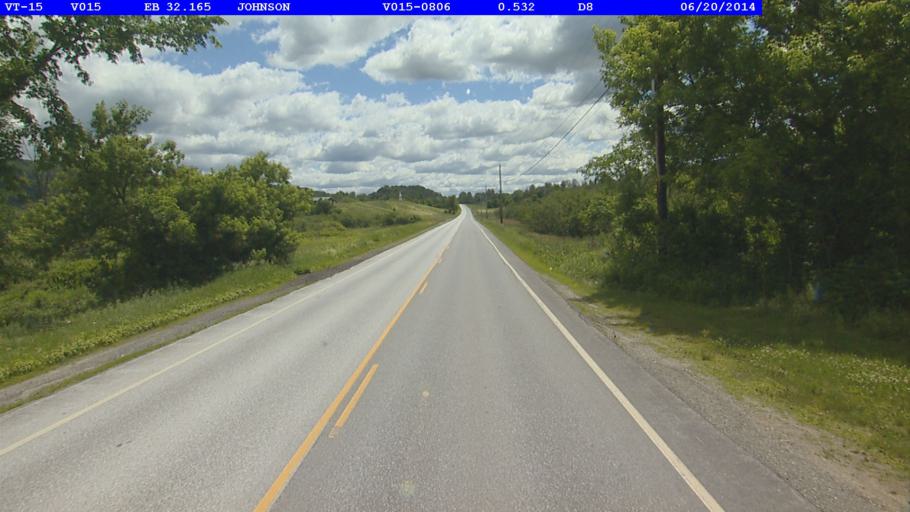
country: US
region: Vermont
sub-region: Lamoille County
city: Johnson
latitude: 44.6490
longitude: -72.7440
